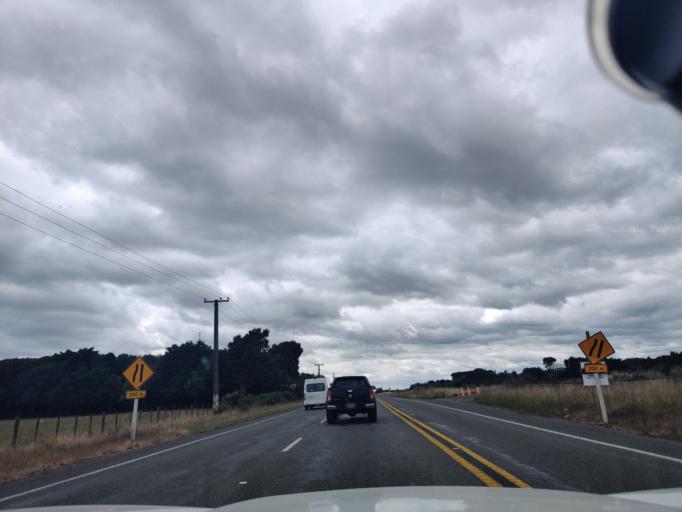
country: NZ
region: Wellington
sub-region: Kapiti Coast District
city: Otaki
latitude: -40.7898
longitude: 175.1312
